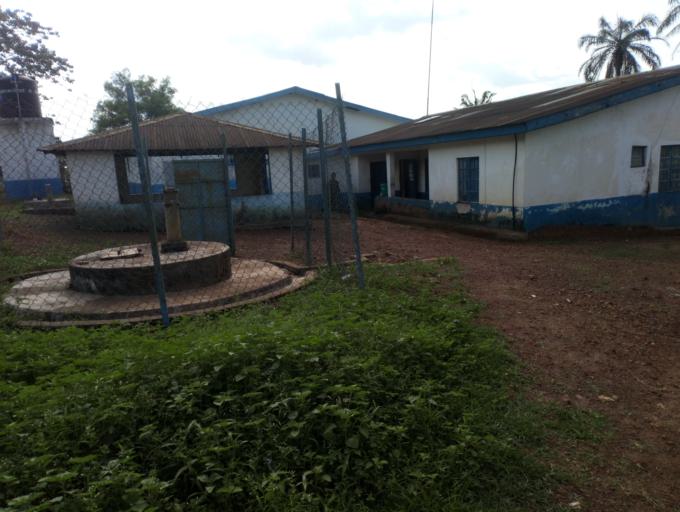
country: SL
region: Southern Province
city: Mogbwemo
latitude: 7.6053
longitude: -12.1735
